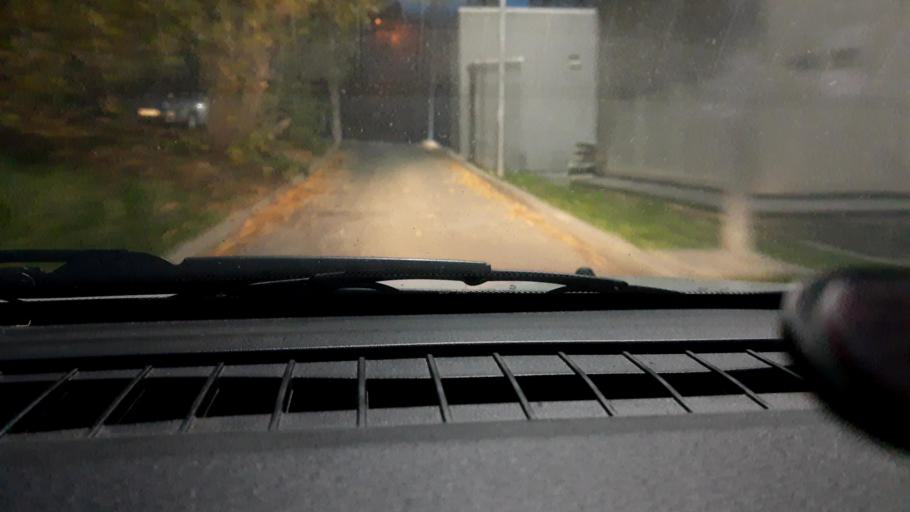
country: RU
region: Nizjnij Novgorod
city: Afonino
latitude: 56.2948
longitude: 44.0649
